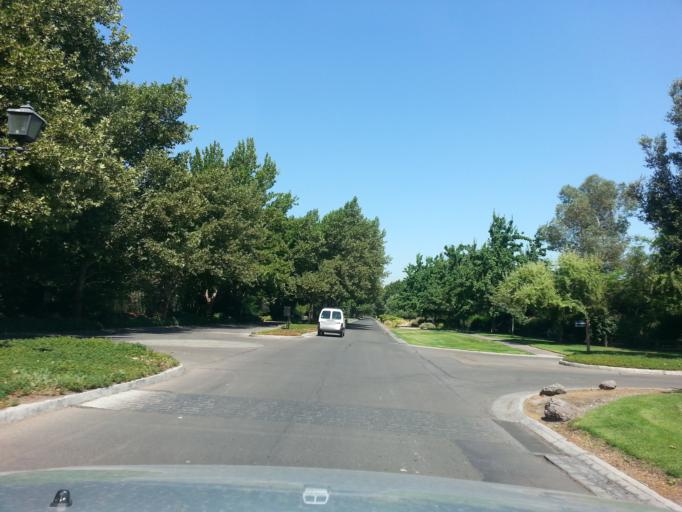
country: CL
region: Santiago Metropolitan
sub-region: Provincia de Chacabuco
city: Chicureo Abajo
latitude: -33.2425
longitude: -70.6869
